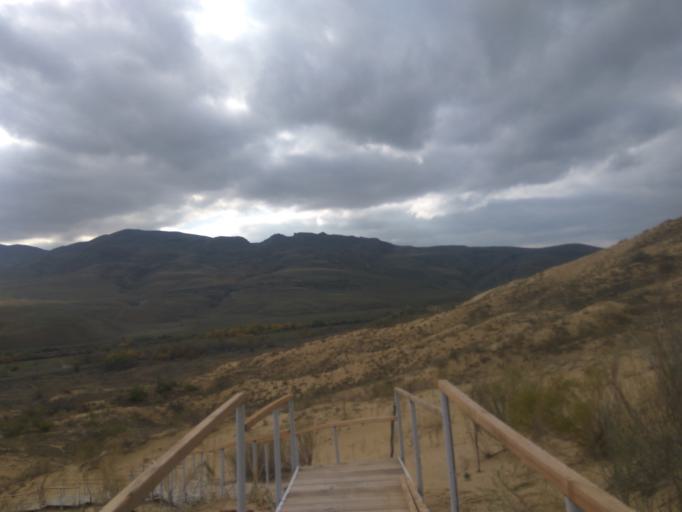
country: RU
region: Dagestan
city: Korkmaskala
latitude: 43.0070
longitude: 47.2343
